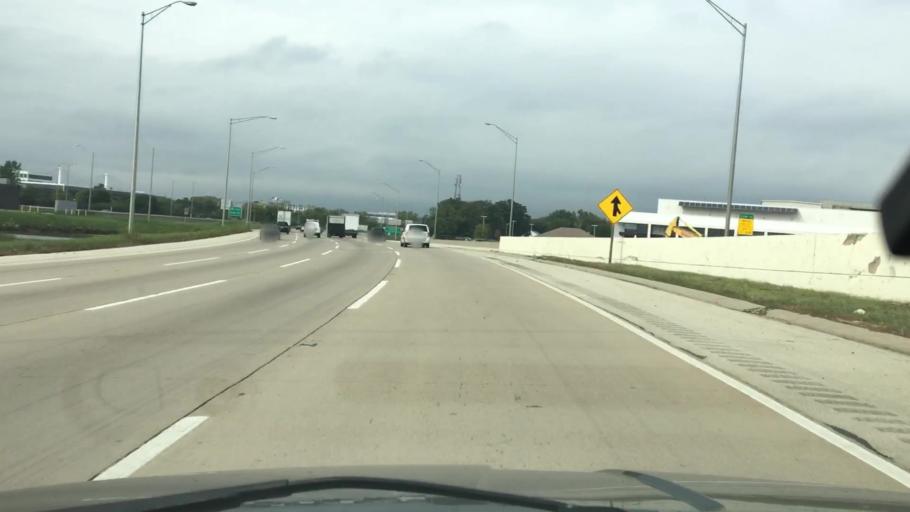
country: US
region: Illinois
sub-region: Lake County
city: Riverwoods
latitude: 42.1550
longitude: -87.8722
